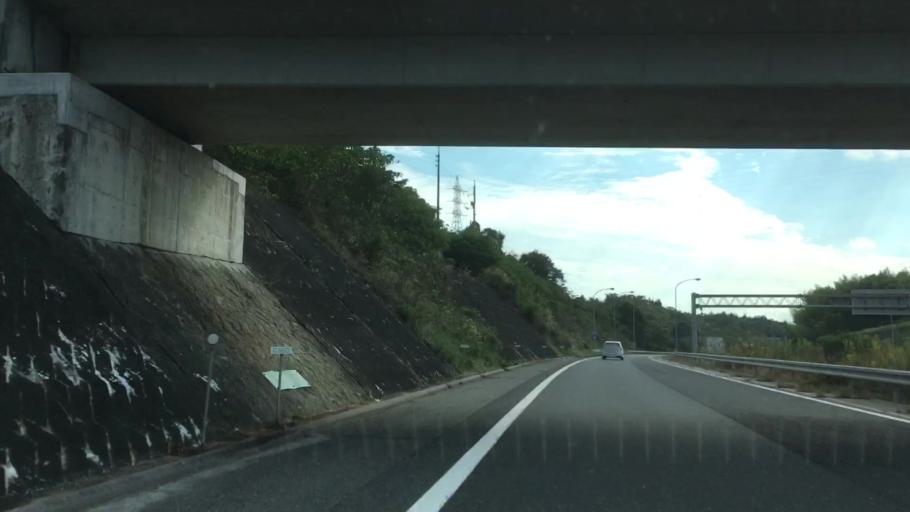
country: JP
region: Hiroshima
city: Hatsukaichi
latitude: 34.3312
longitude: 132.2944
